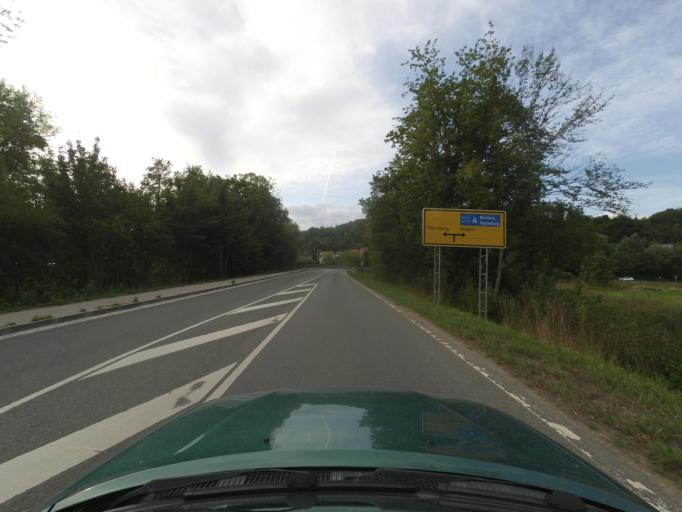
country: DE
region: Bavaria
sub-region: Regierungsbezirk Mittelfranken
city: Burgthann
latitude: 49.3580
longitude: 11.3224
